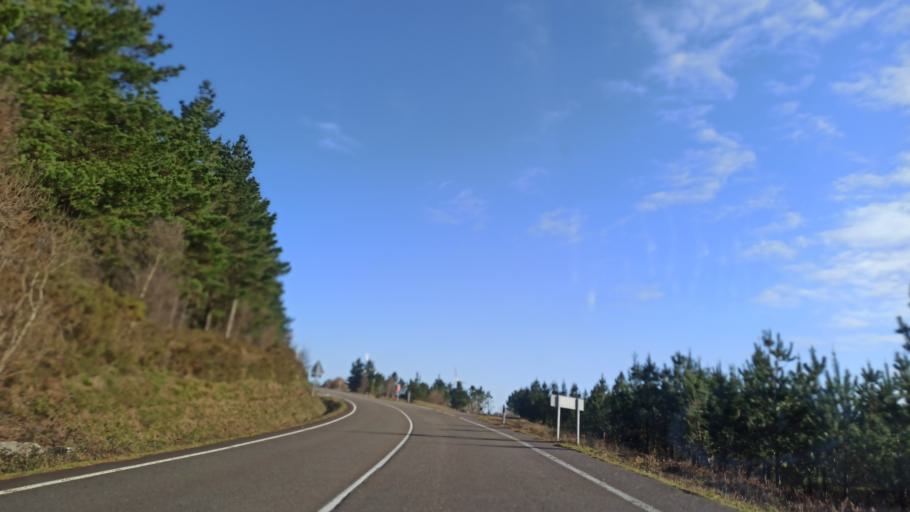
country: ES
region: Galicia
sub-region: Provincia da Coruna
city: As Pontes de Garcia Rodriguez
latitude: 43.5028
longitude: -7.8222
